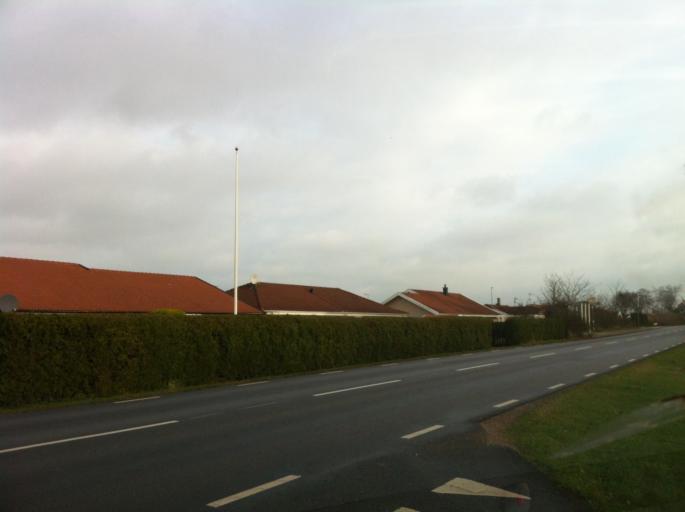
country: SE
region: Skane
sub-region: Landskrona
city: Asmundtorp
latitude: 55.8874
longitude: 12.9591
